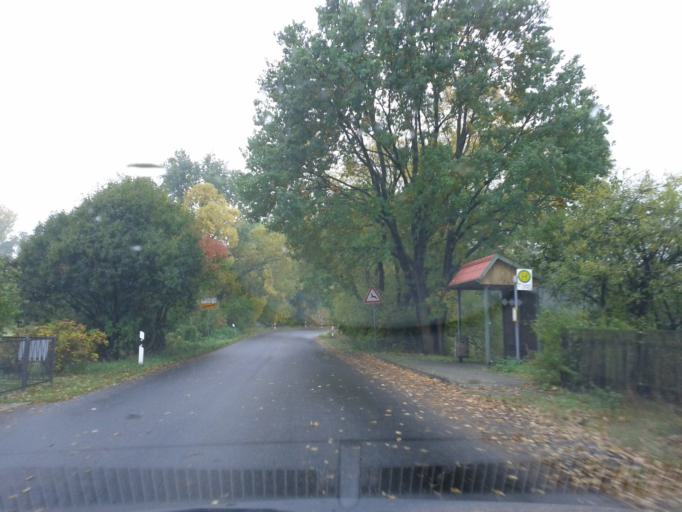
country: DE
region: Brandenburg
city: Spreenhagen
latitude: 52.3965
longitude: 13.9003
